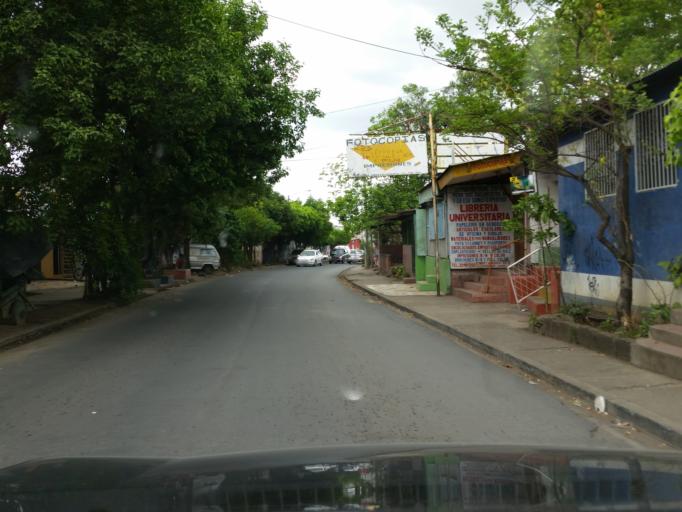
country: NI
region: Managua
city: Managua
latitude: 12.1384
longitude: -86.2239
